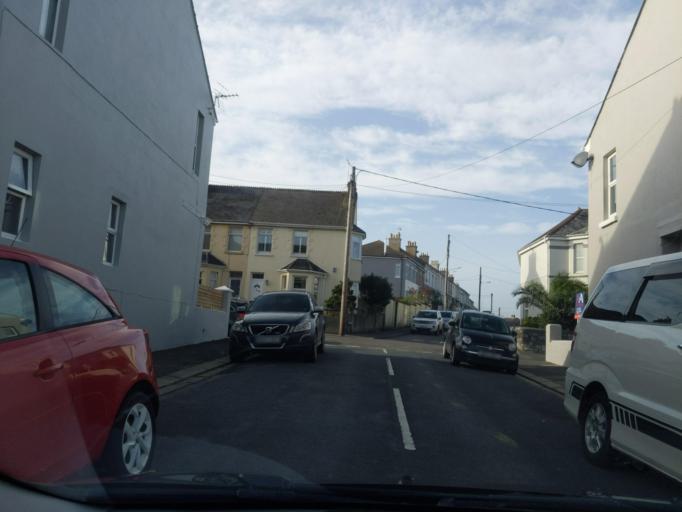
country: GB
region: England
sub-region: Cornwall
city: Torpoint
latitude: 50.3754
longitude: -4.1979
